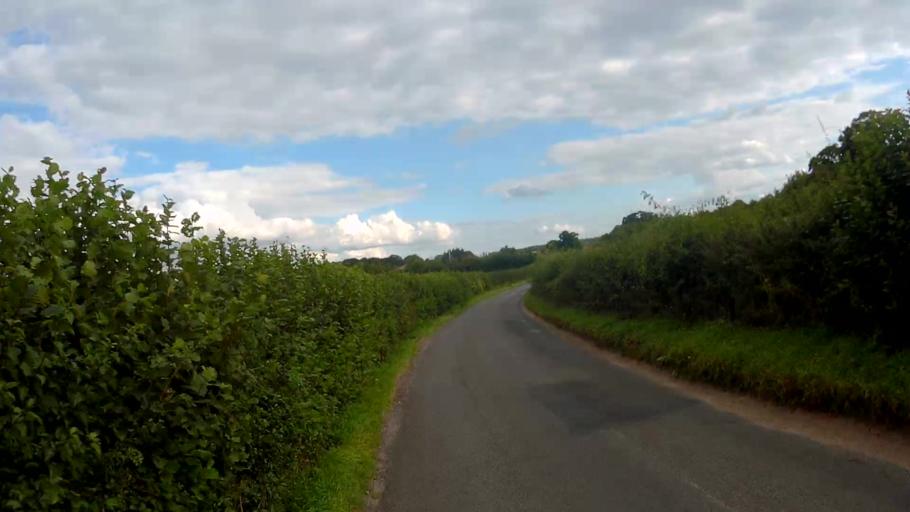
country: GB
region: England
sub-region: Hampshire
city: Kings Worthy
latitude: 51.1473
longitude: -1.2190
